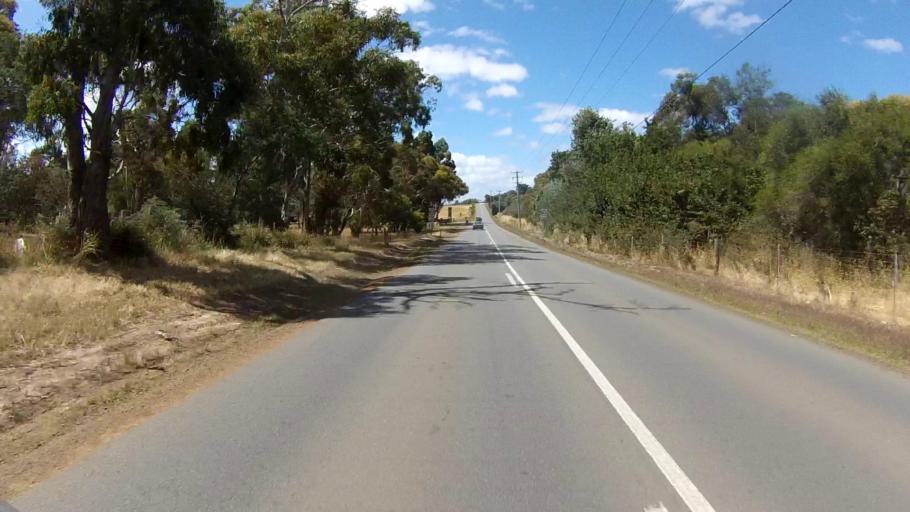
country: AU
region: Tasmania
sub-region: Clarence
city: Cambridge
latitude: -42.8214
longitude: 147.4429
